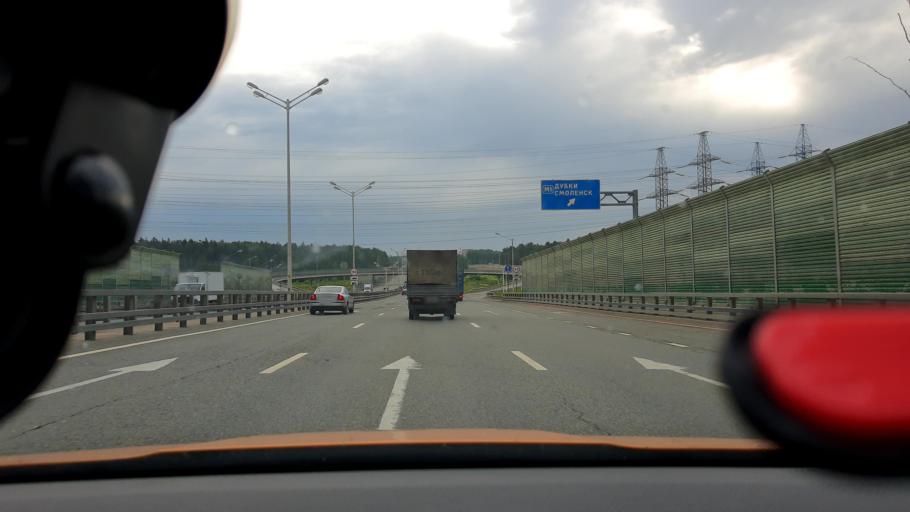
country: RU
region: Moskovskaya
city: Lesnoy Gorodok
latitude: 55.6380
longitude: 37.2267
